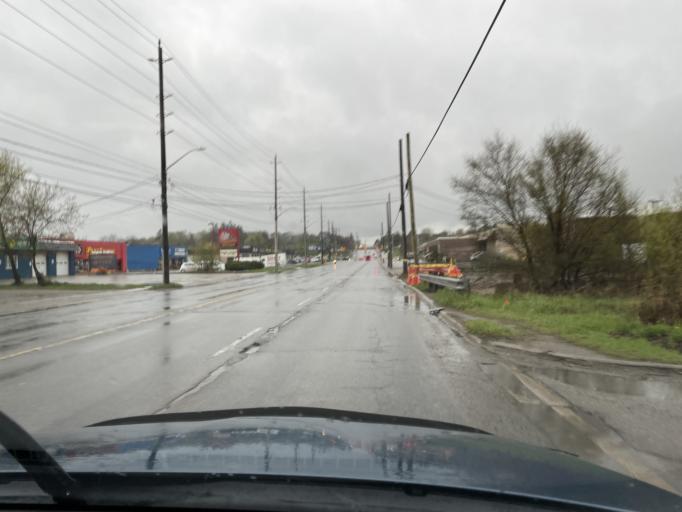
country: CA
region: Ontario
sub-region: Wellington County
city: Guelph
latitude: 43.5539
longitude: -80.2266
